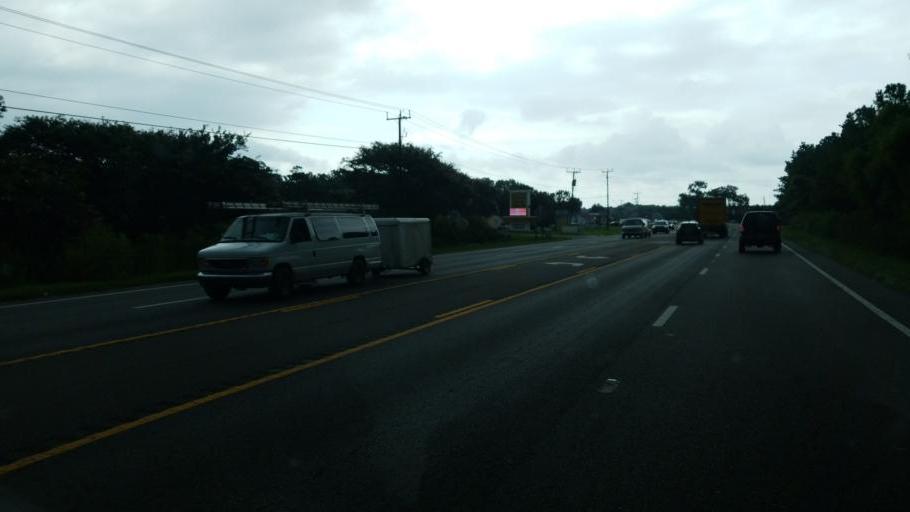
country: US
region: North Carolina
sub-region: Dare County
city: Southern Shores
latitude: 36.0945
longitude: -75.8106
